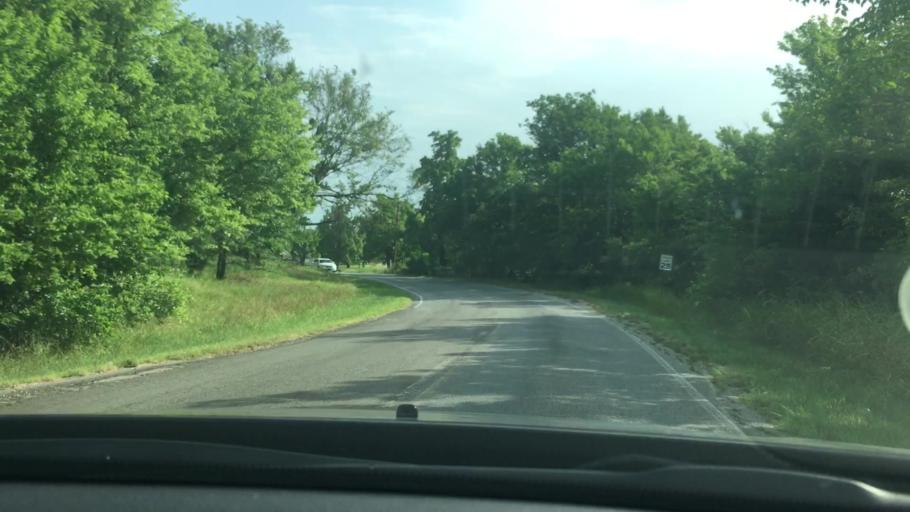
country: US
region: Oklahoma
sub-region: Pontotoc County
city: Byng
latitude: 34.8705
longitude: -96.5965
